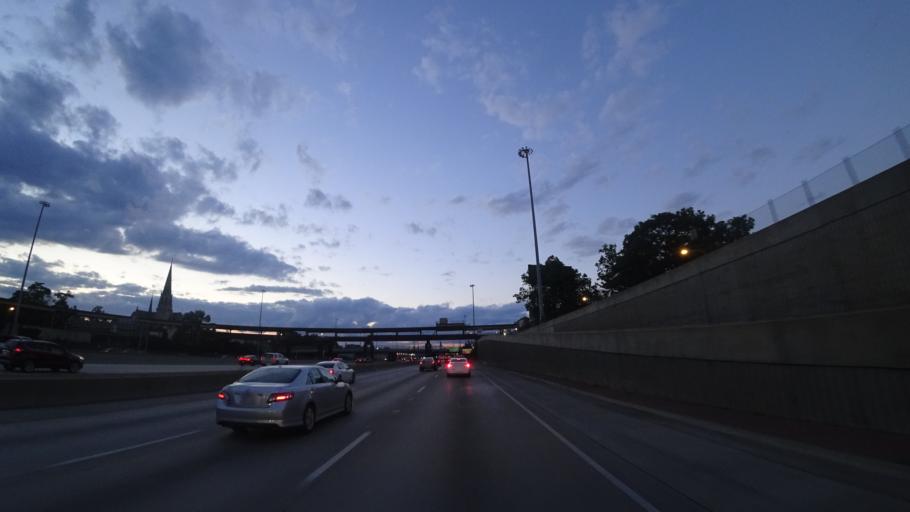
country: US
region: Illinois
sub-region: Cook County
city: Chicago
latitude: 41.7853
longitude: -87.6305
